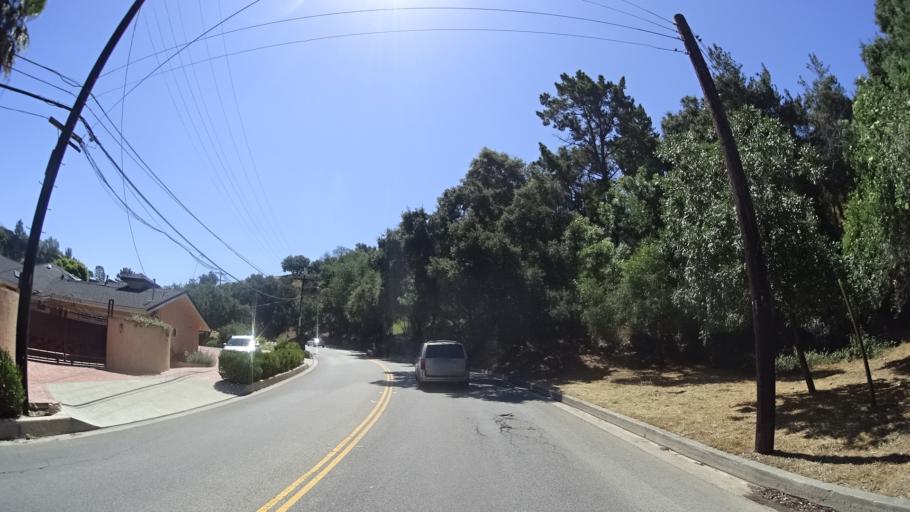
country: US
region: California
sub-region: Los Angeles County
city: Sherman Oaks
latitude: 34.1340
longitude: -118.4510
